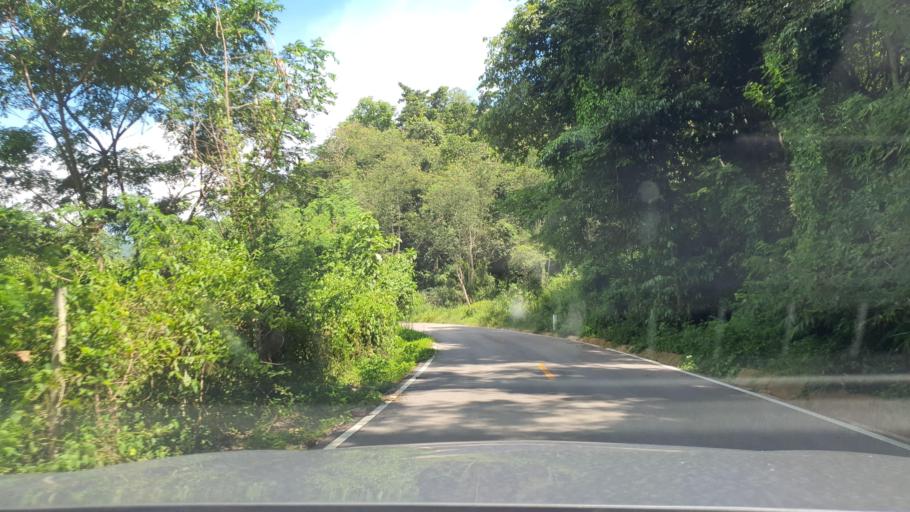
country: TH
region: Chiang Mai
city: Mae On
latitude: 18.7176
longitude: 99.2313
